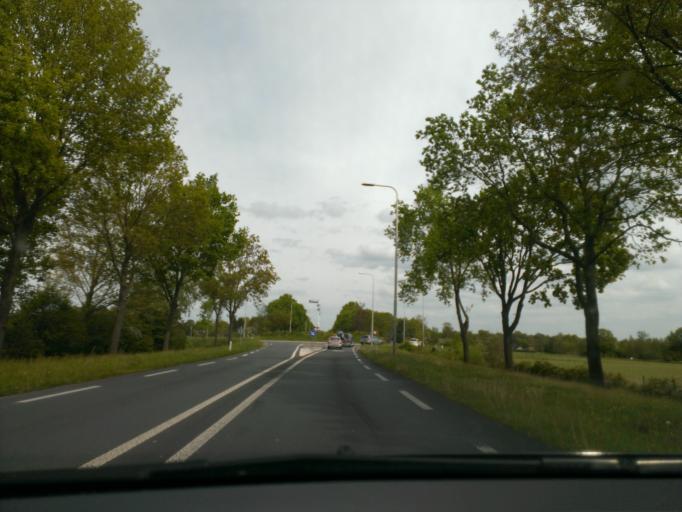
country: NL
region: Gelderland
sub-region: Gemeente Epe
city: Epe
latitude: 52.3359
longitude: 5.9956
